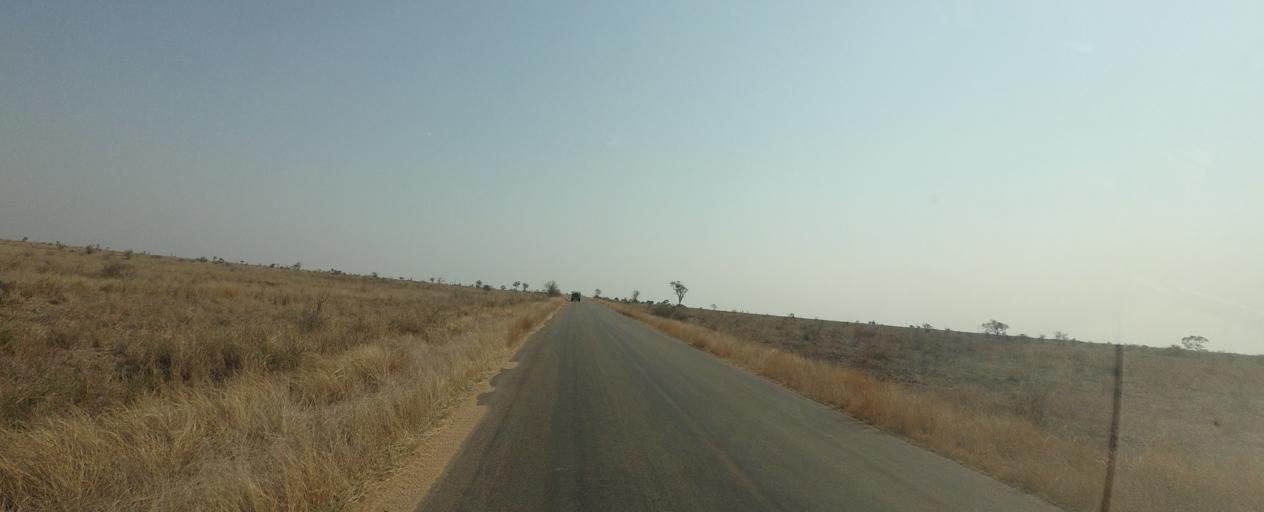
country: ZA
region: Limpopo
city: Thulamahashi
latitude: -24.3592
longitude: 31.7637
